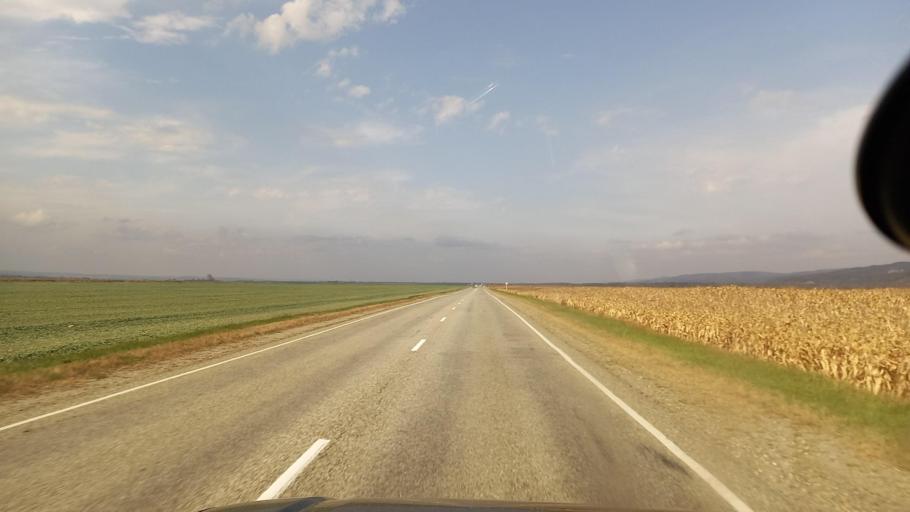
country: RU
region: Krasnodarskiy
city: Shedok
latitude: 44.2970
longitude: 40.8631
